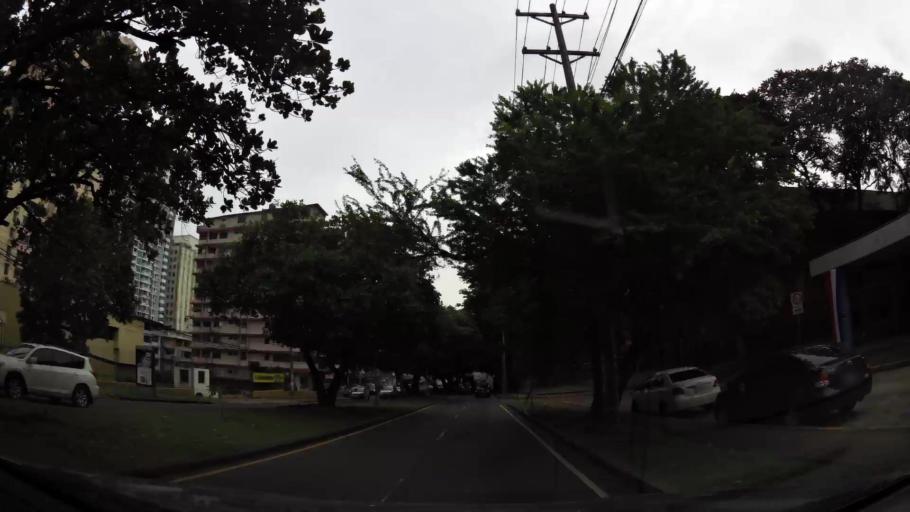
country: PA
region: Panama
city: Panama
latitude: 8.9850
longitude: -79.5310
